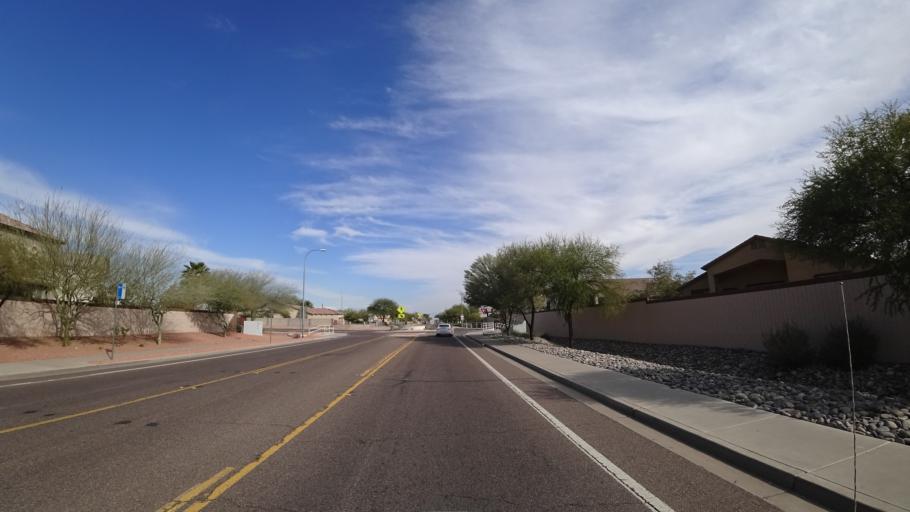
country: US
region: Arizona
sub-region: Maricopa County
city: Avondale
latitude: 33.4281
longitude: -112.3031
